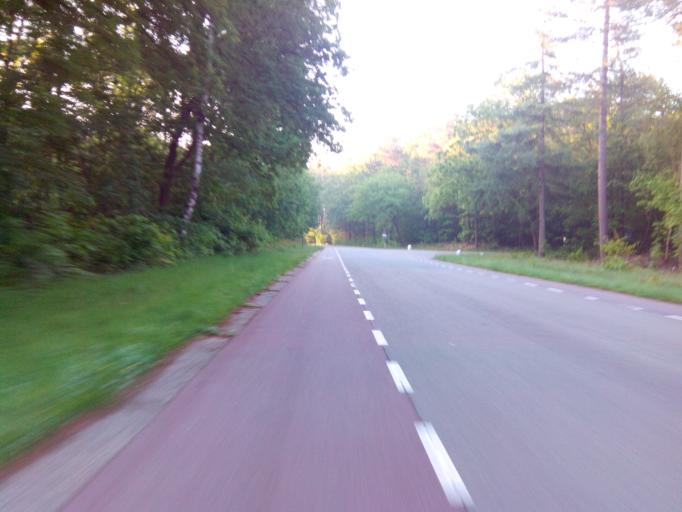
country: NL
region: Utrecht
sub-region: Gemeente Amersfoort
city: Amersfoort
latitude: 52.1272
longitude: 5.3355
